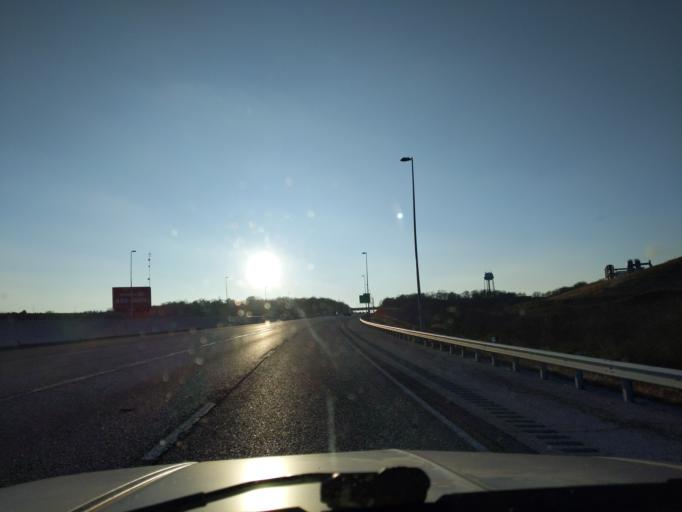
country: US
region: Oklahoma
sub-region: Creek County
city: Sapulpa
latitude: 36.0146
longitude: -96.1023
